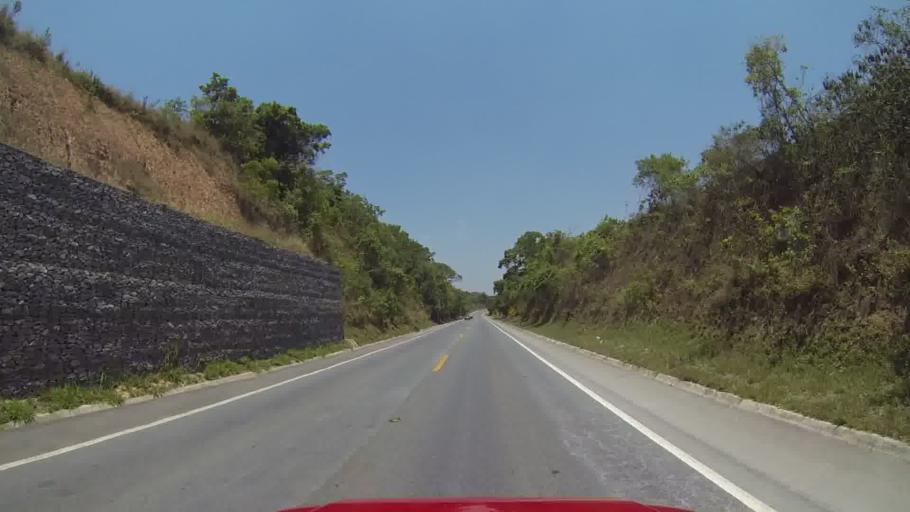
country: BR
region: Minas Gerais
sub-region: Itapecerica
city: Itapecerica
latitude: -20.3224
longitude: -45.2208
